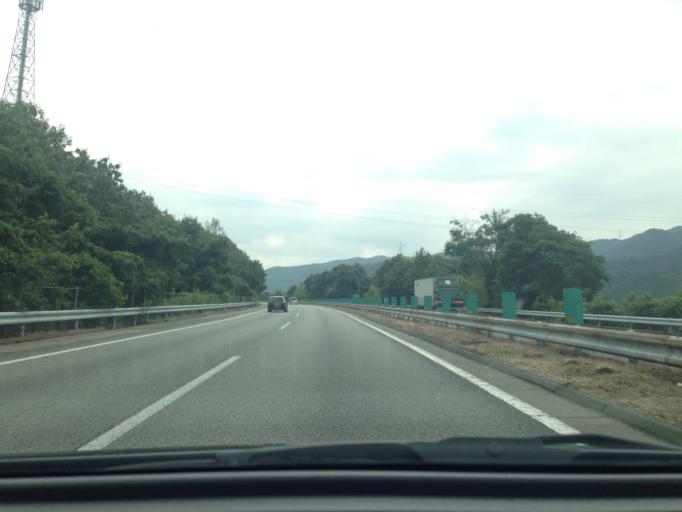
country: JP
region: Aichi
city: Shinshiro
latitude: 34.8448
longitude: 137.4761
